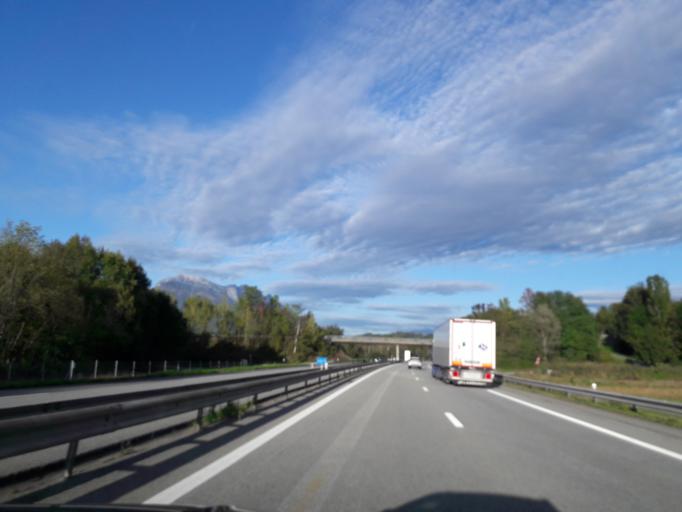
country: FR
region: Rhone-Alpes
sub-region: Departement de la Savoie
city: Cruet
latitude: 45.5049
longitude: 6.0845
